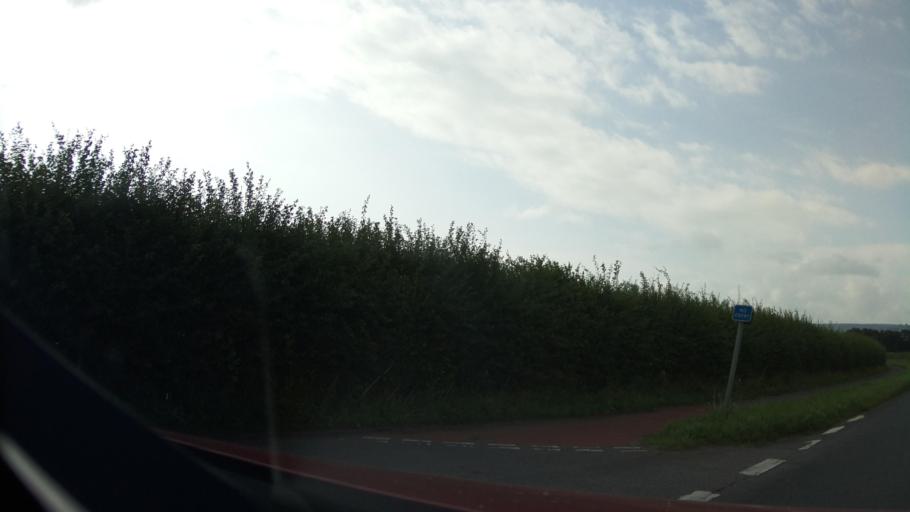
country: GB
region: England
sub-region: Bath and North East Somerset
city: Compton Martin
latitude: 51.3306
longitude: -2.6413
